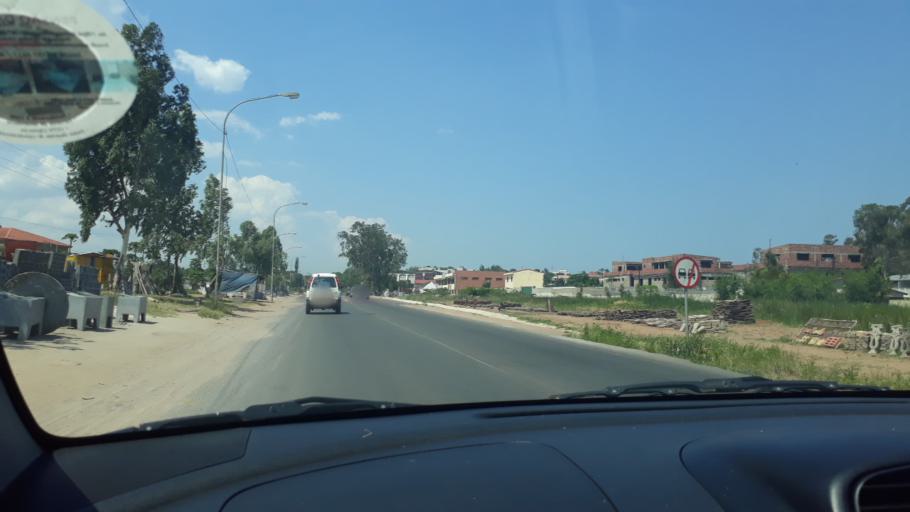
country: MZ
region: Maputo
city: Matola
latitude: -25.9693
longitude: 32.4423
